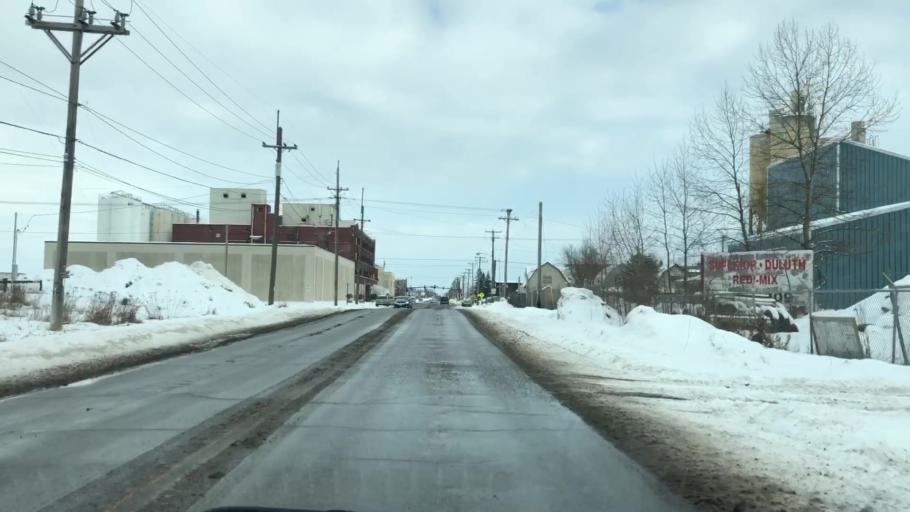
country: US
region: Wisconsin
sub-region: Douglas County
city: Superior
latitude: 46.7279
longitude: -92.1083
